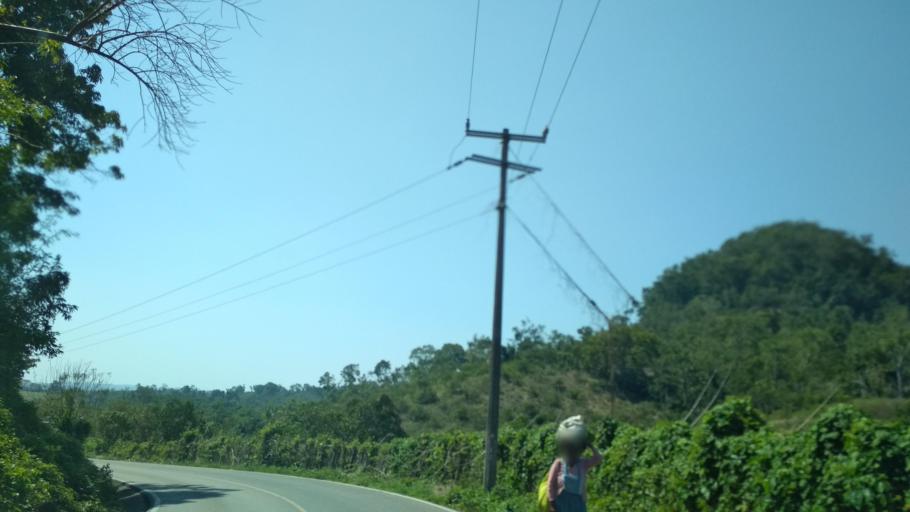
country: MX
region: Veracruz
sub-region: Papantla
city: Polutla
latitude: 20.4733
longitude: -97.2176
